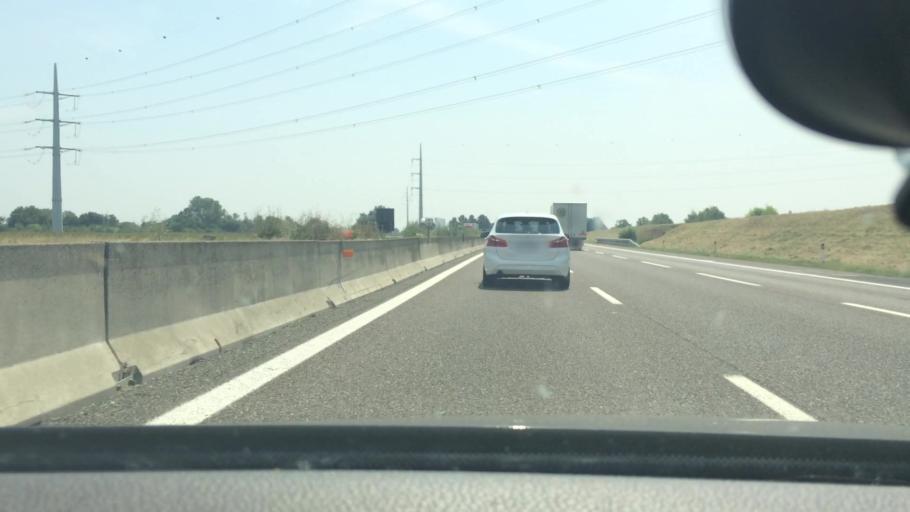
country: IT
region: Lombardy
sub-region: Provincia di Lodi
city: Fombio
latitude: 45.1269
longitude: 9.6632
